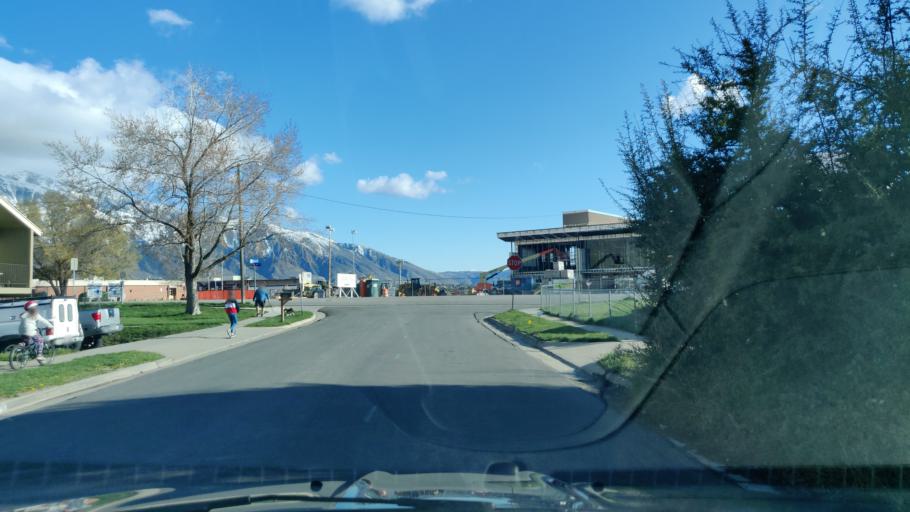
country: US
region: Utah
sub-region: Salt Lake County
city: Little Cottonwood Creek Valley
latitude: 40.6136
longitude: -111.8275
